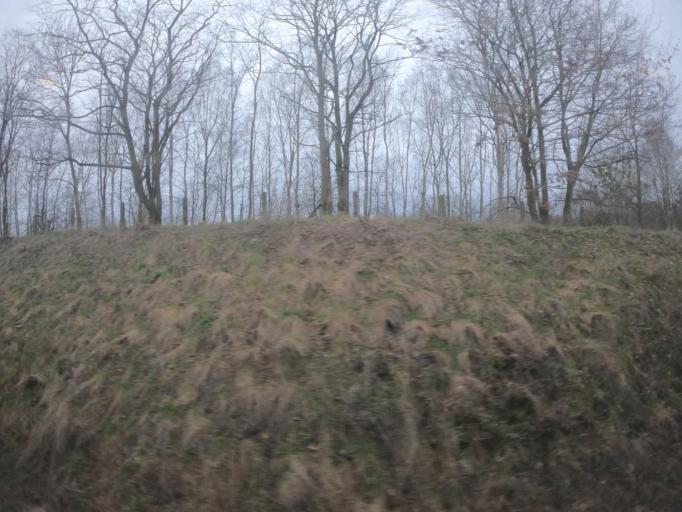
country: PL
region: West Pomeranian Voivodeship
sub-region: Powiat szczecinecki
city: Szczecinek
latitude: 53.6881
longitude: 16.6956
